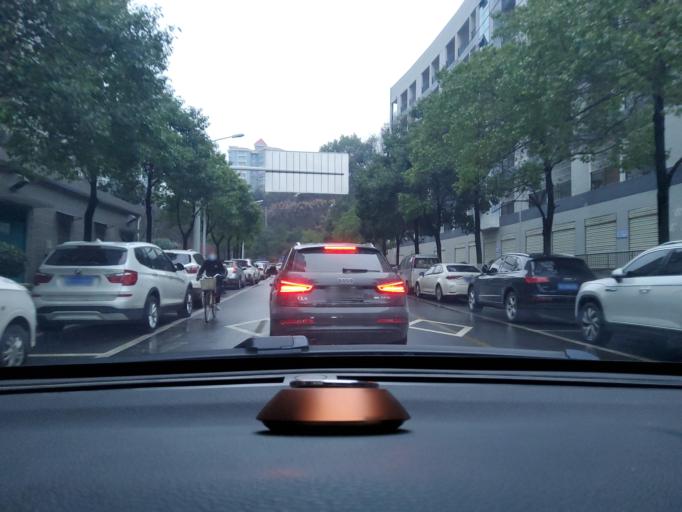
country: CN
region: Hubei
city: Tuanchengshan
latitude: 30.1893
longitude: 115.0272
